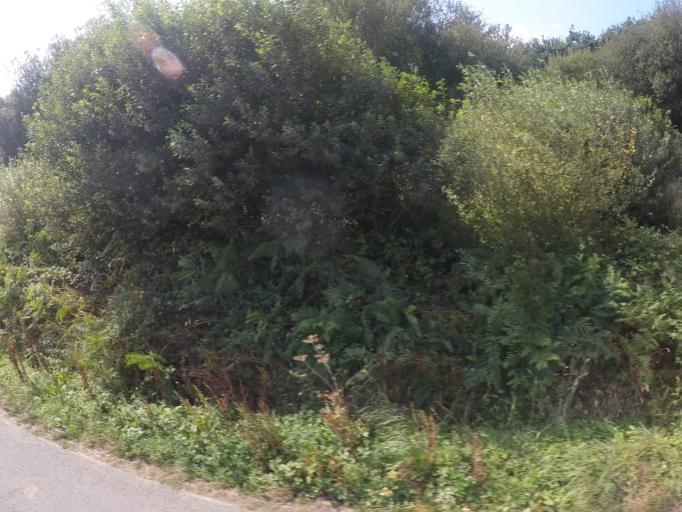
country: FR
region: Brittany
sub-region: Departement des Cotes-d'Armor
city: Tremuson
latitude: 48.5444
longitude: -2.8905
